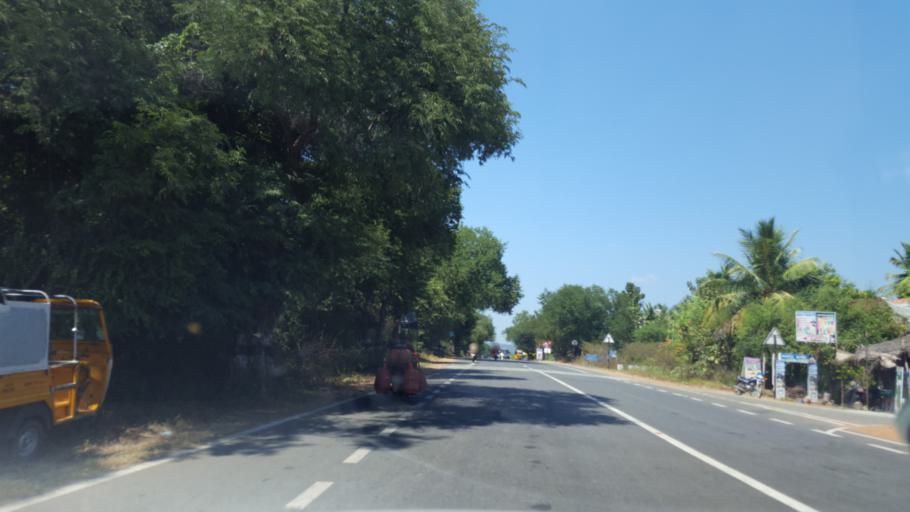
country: IN
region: Tamil Nadu
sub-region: Kancheepuram
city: Karumbakkam
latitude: 12.6253
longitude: 80.0521
